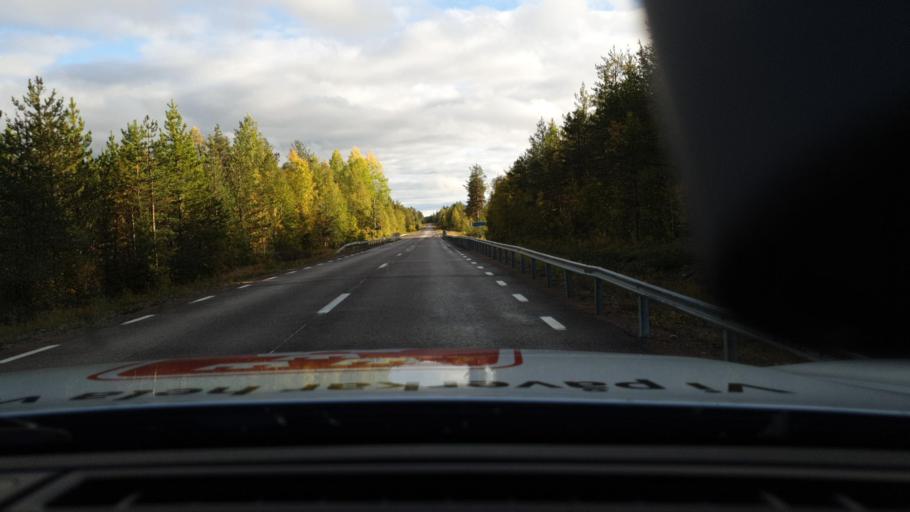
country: SE
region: Norrbotten
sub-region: Overkalix Kommun
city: OEverkalix
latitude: 66.6942
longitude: 22.6703
